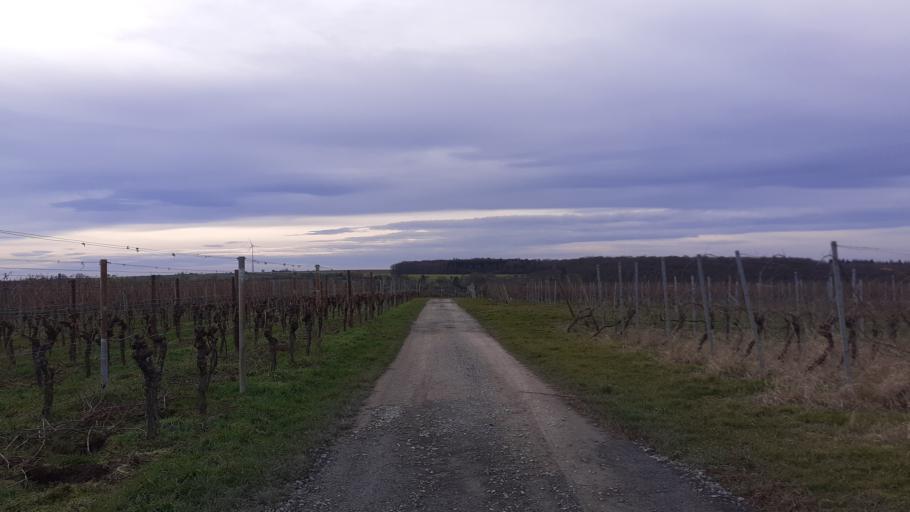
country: DE
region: Baden-Wuerttemberg
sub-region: Regierungsbezirk Stuttgart
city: Mundelsheim
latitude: 48.9863
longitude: 9.2158
